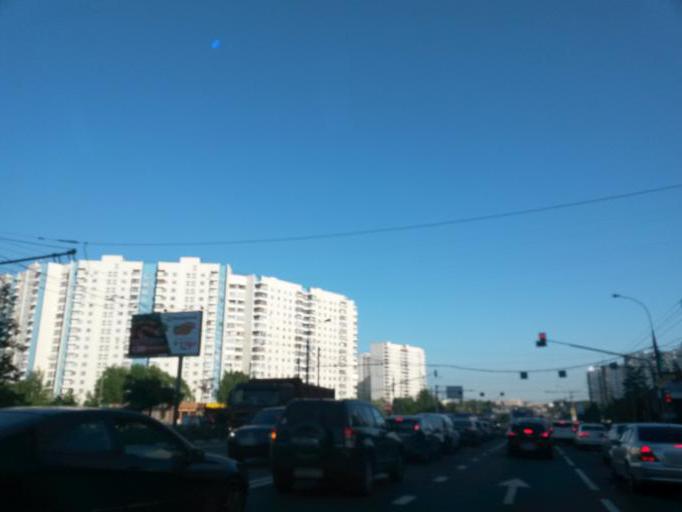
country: RU
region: Moscow
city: Biryulevo
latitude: 55.5837
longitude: 37.6799
